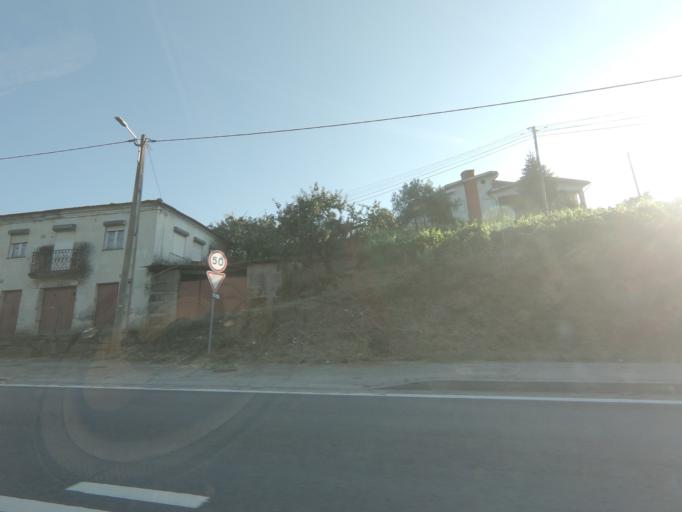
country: PT
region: Vila Real
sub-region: Vila Real
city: Vila Real
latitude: 41.2864
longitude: -7.7027
